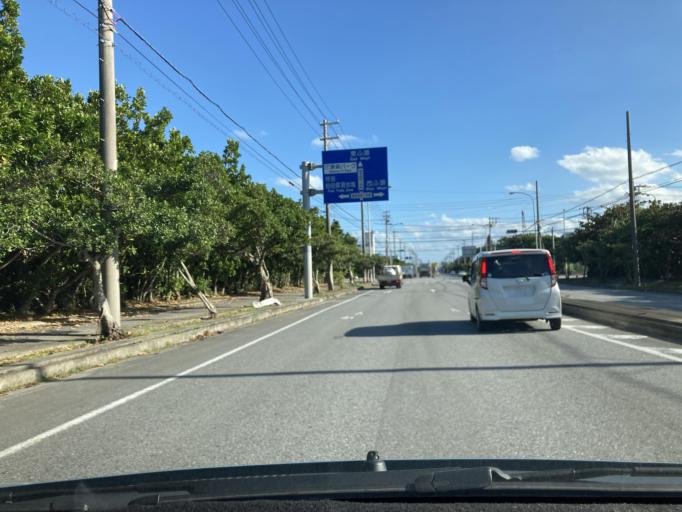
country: JP
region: Okinawa
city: Katsuren-haebaru
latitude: 26.3360
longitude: 127.8491
